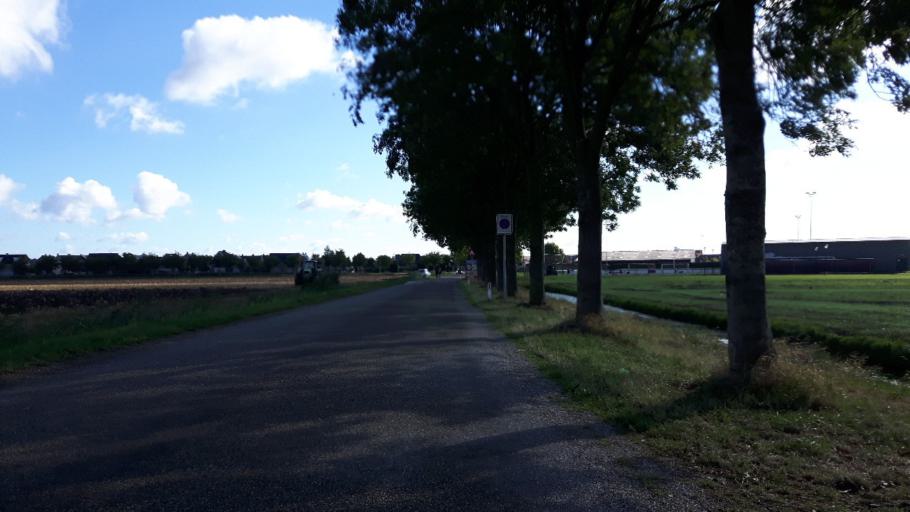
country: NL
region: Gelderland
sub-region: Gemeente Culemborg
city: Culemborg
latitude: 51.9507
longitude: 5.1946
